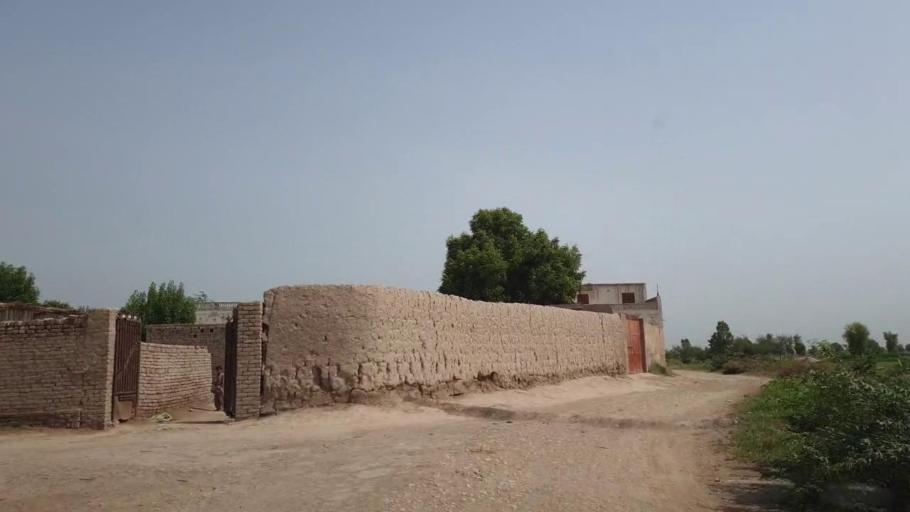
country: PK
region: Sindh
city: Sakrand
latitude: 26.1239
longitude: 68.3697
